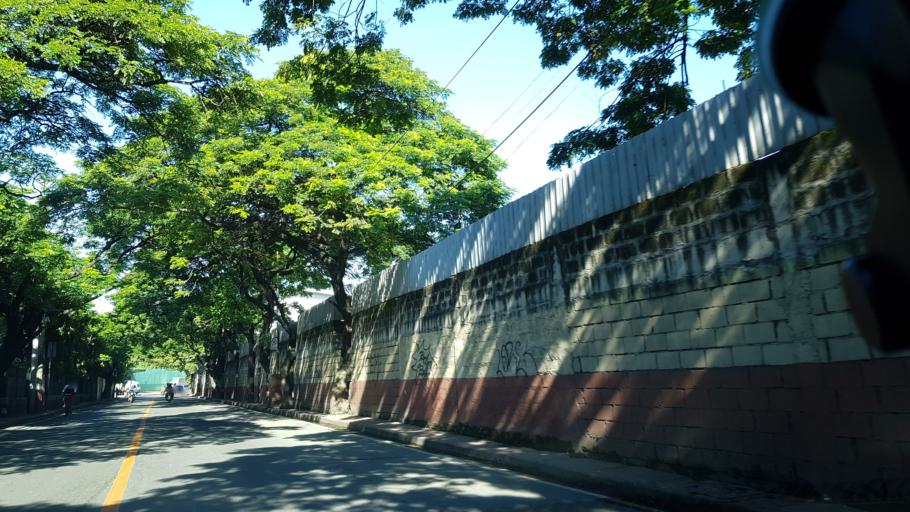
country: PH
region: Metro Manila
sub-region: Pasig
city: Pasig City
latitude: 14.5757
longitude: 121.0884
